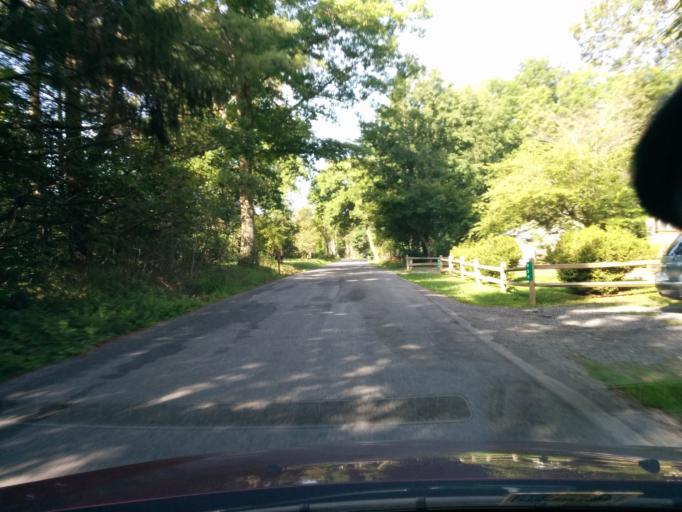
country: US
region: Virginia
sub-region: City of Lexington
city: Lexington
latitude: 37.7779
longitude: -79.4646
